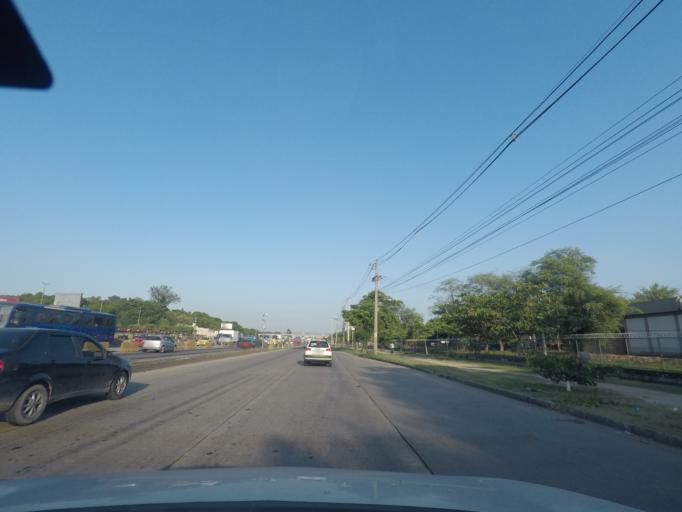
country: BR
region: Rio de Janeiro
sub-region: Duque De Caxias
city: Duque de Caxias
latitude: -22.8345
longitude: -43.2621
